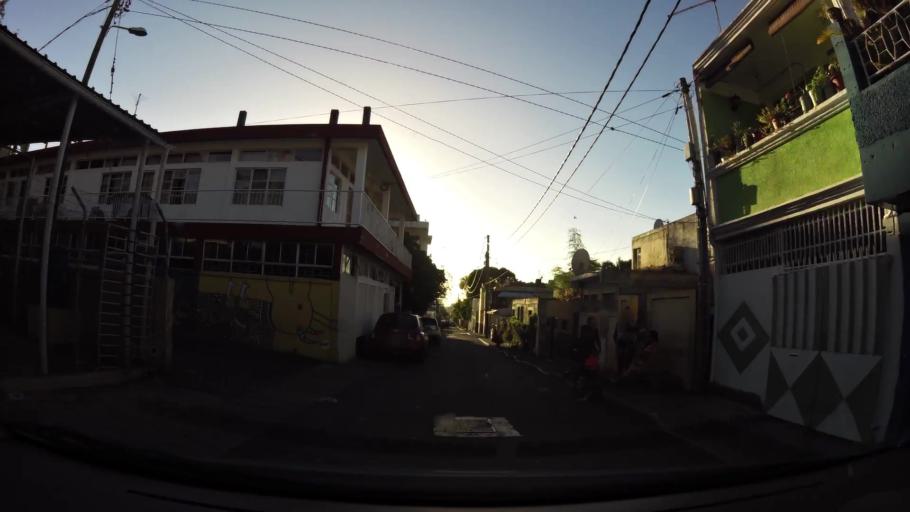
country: MU
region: Port Louis
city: Port Louis
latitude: -20.1769
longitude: 57.5127
